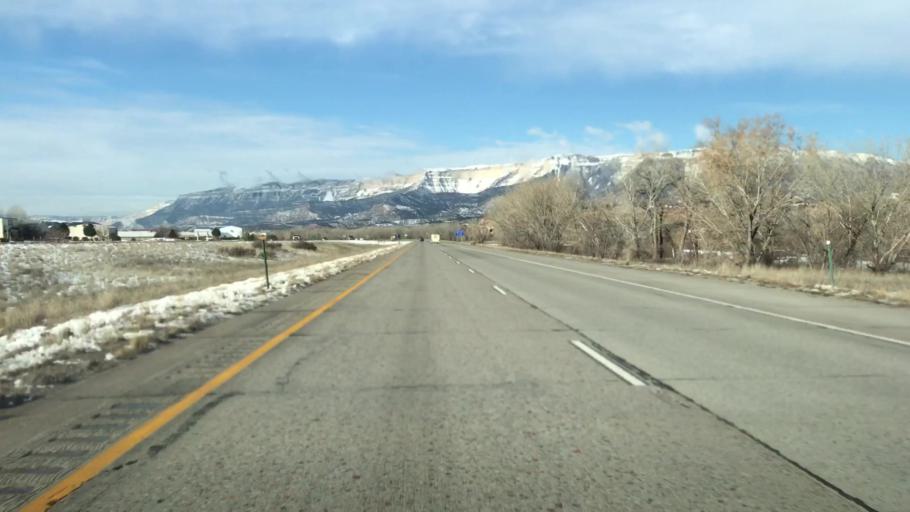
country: US
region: Colorado
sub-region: Garfield County
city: Rifle
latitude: 39.5255
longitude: -107.7593
